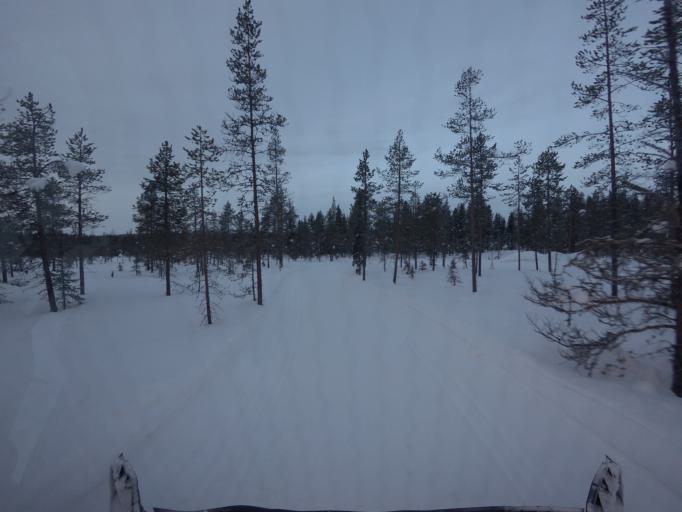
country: FI
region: Lapland
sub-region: Tunturi-Lappi
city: Kolari
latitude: 67.6220
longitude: 24.1437
